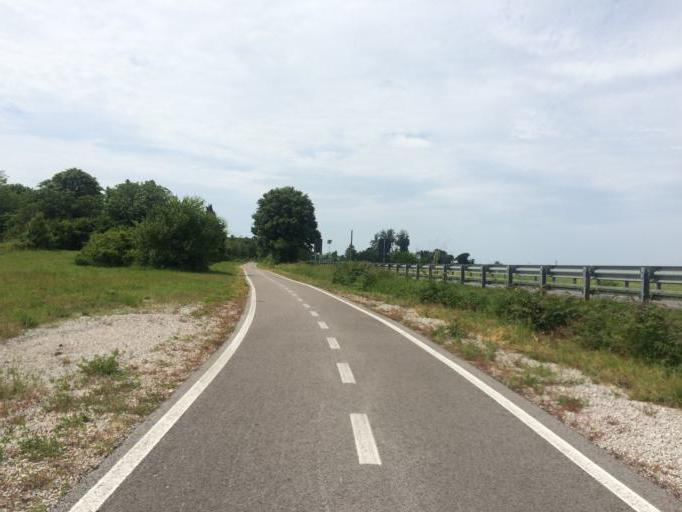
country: IT
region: Friuli Venezia Giulia
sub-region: Provincia di Udine
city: Aquileia
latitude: 45.7307
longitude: 13.3887
